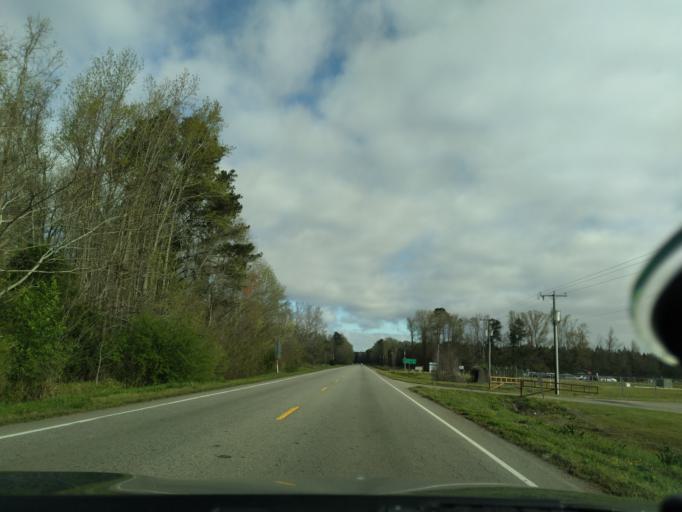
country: US
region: North Carolina
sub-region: Washington County
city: Plymouth
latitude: 35.8733
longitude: -76.6942
